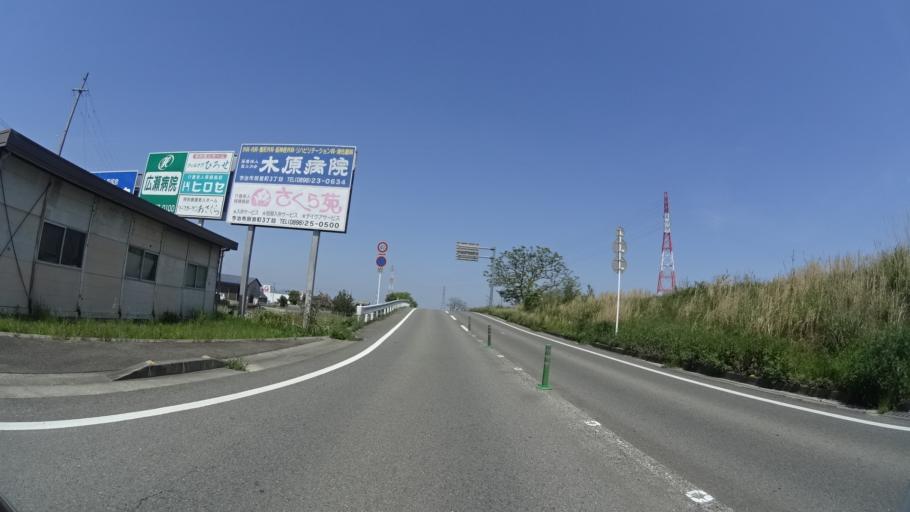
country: JP
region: Ehime
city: Hojo
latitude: 34.0348
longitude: 132.9715
